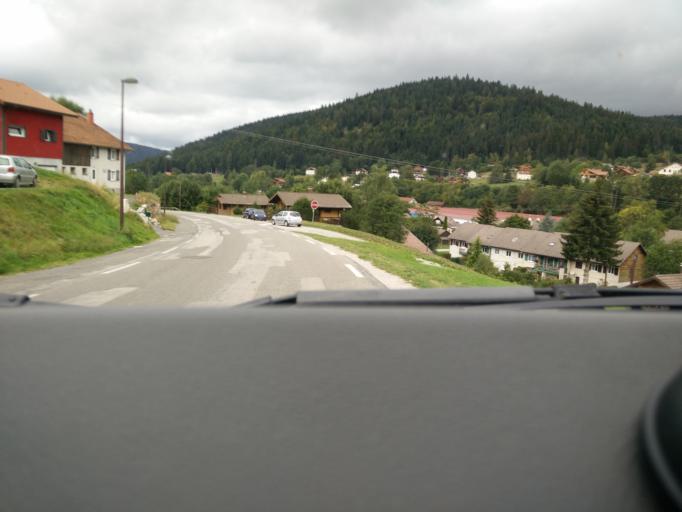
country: FR
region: Lorraine
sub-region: Departement des Vosges
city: Xonrupt-Longemer
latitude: 48.0815
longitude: 6.9325
